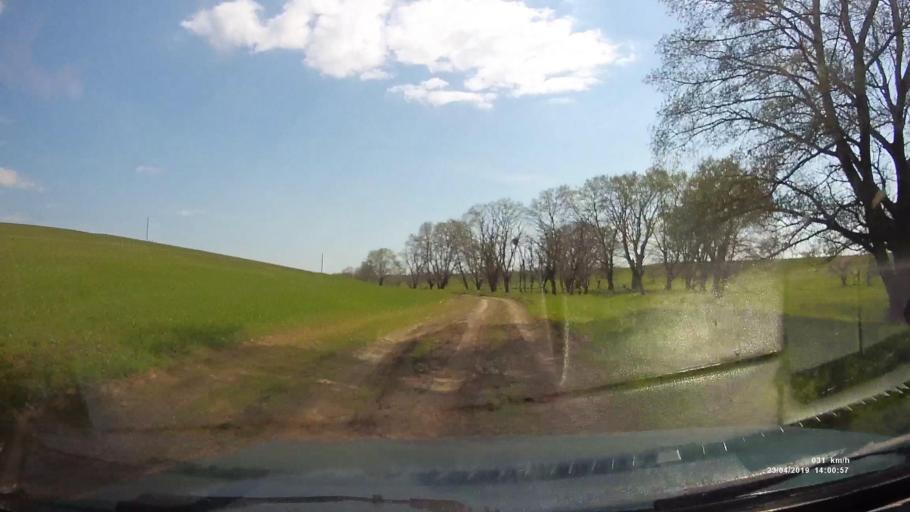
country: RU
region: Rostov
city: Remontnoye
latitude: 46.5571
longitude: 42.9475
